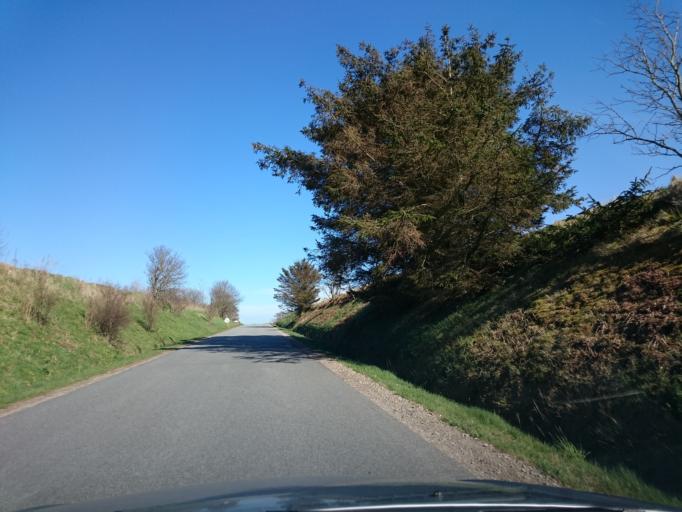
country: DK
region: North Denmark
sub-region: Hjorring Kommune
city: Hjorring
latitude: 57.5248
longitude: 9.9781
